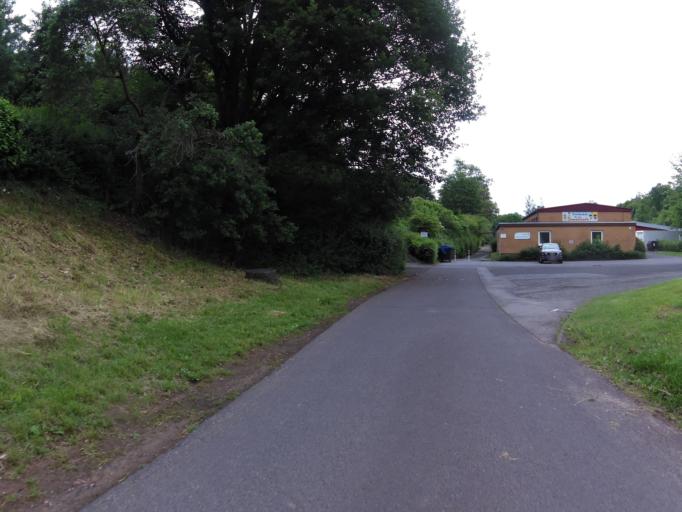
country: DE
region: Hesse
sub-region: Regierungsbezirk Kassel
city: Bad Hersfeld
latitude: 50.8702
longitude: 9.6803
